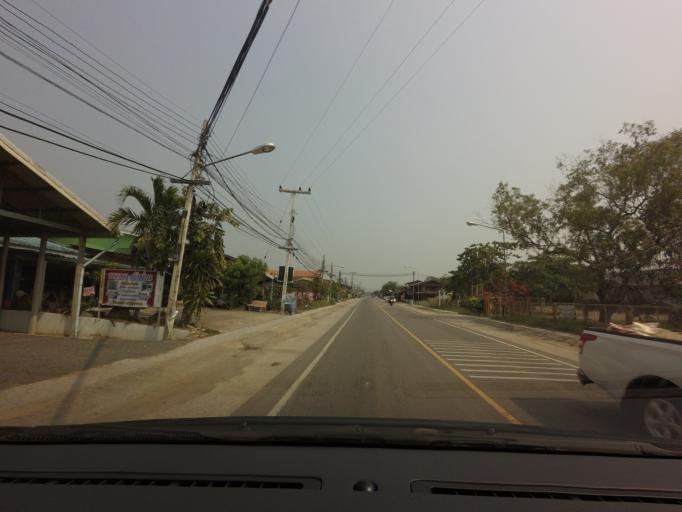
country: TH
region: Prachuap Khiri Khan
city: Kui Buri
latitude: 12.0681
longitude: 99.8734
